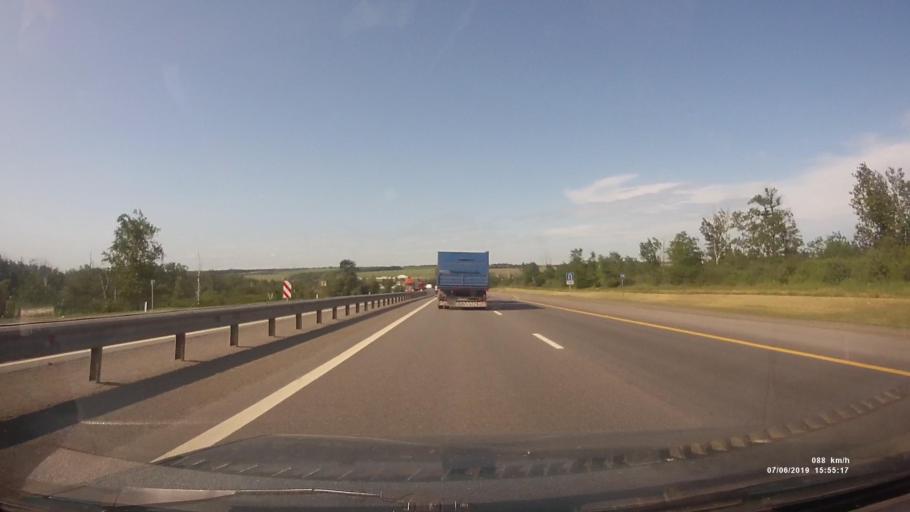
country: RU
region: Rostov
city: Gornyy
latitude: 47.8737
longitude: 40.2080
